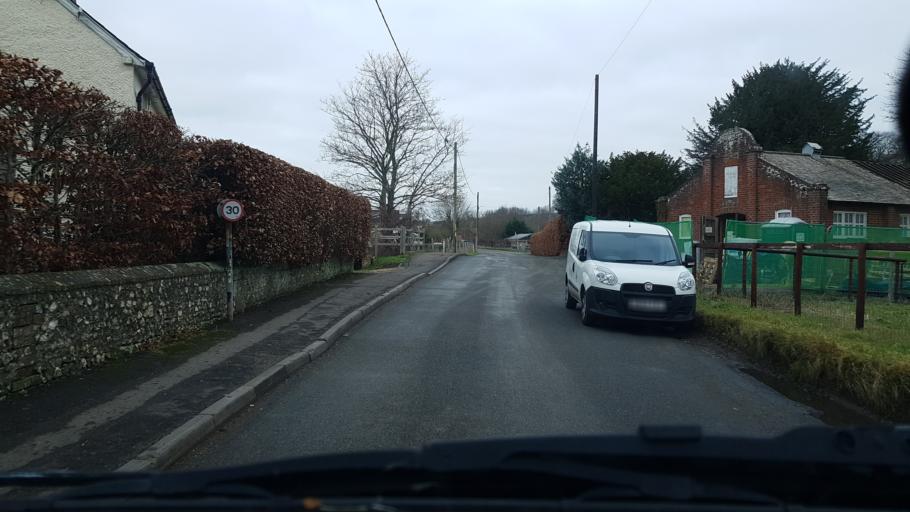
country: GB
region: England
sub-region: Hampshire
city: Andover
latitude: 51.2774
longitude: -1.4537
